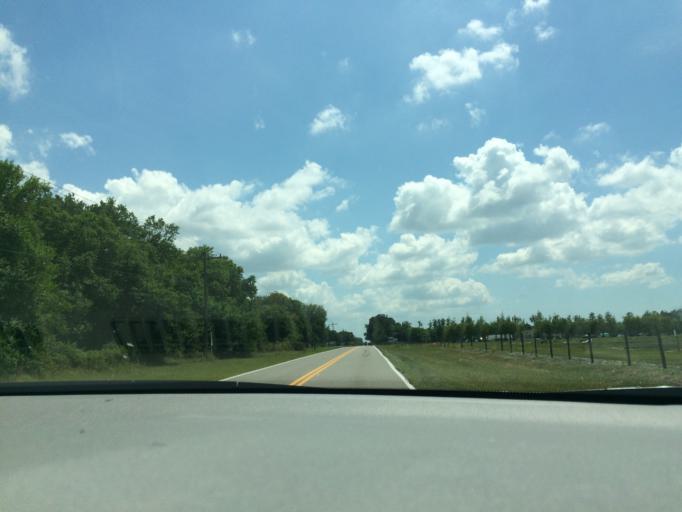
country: US
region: Florida
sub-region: Sarasota County
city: The Meadows
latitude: 27.4587
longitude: -82.3955
